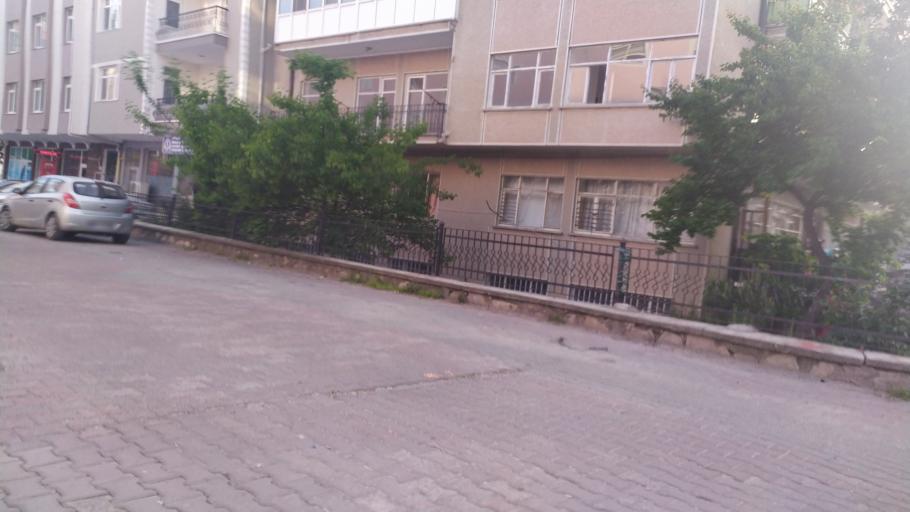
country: TR
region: Kirsehir
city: Kirsehir
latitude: 39.1509
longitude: 34.1593
